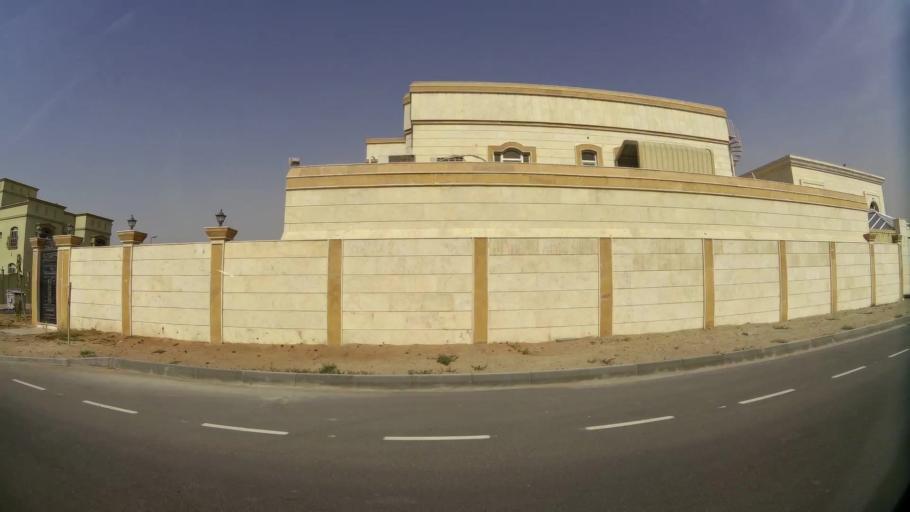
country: AE
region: Ash Shariqah
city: Sharjah
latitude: 25.2620
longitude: 55.4575
